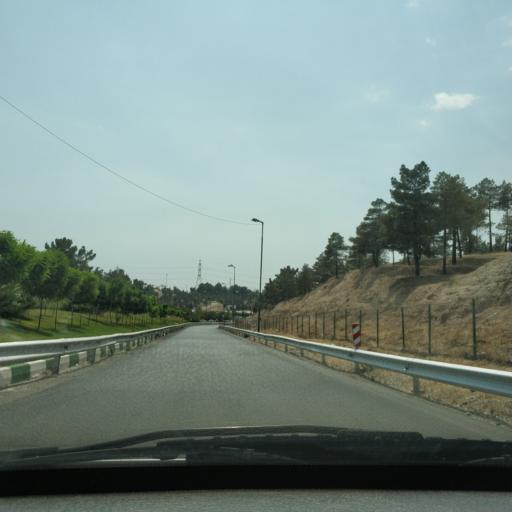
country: IR
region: Tehran
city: Tajrish
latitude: 35.7716
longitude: 51.5564
